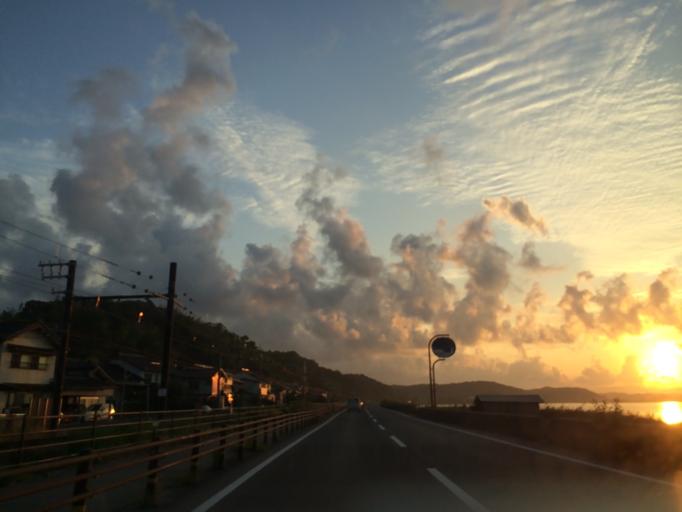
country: JP
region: Shimane
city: Matsue-shi
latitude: 35.4776
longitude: 132.9578
